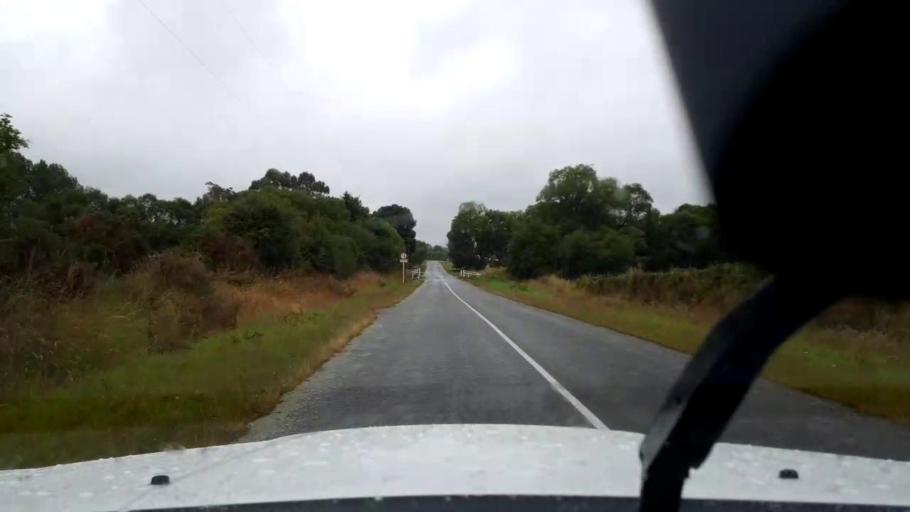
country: NZ
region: Canterbury
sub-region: Timaru District
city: Pleasant Point
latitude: -44.2524
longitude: 171.2549
